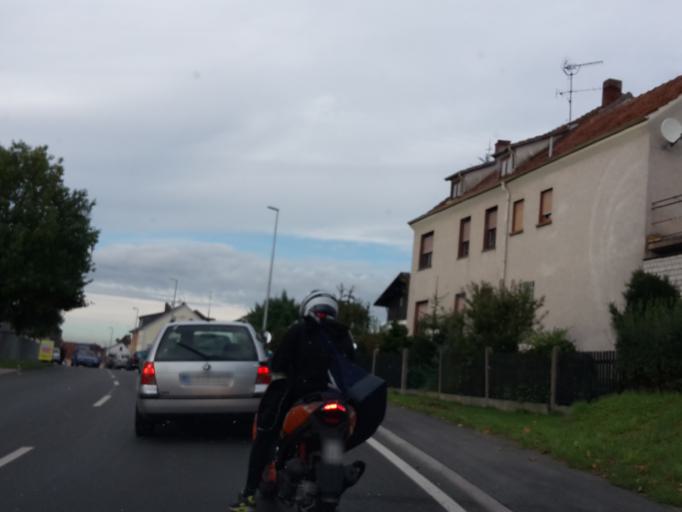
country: DE
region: Hesse
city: Bad Camberg
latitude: 50.2813
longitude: 8.2805
